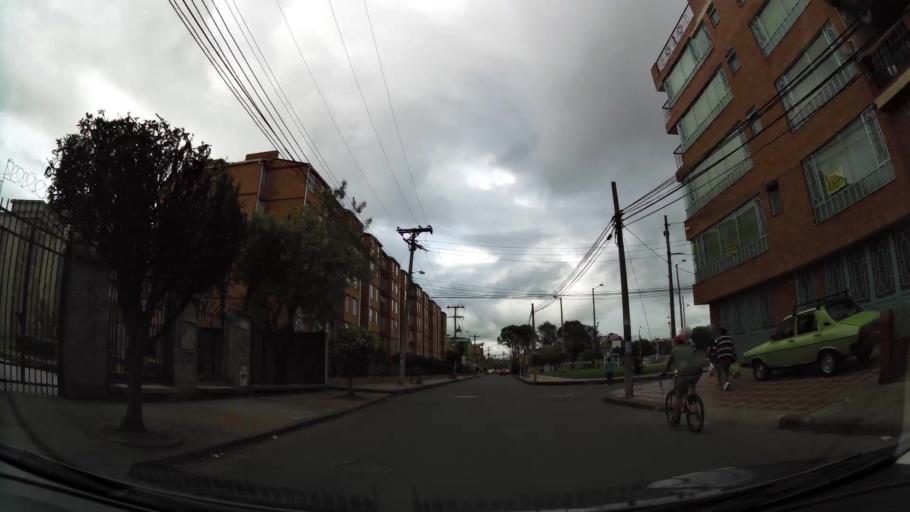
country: CO
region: Bogota D.C.
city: Barrio San Luis
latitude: 4.6999
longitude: -74.1070
